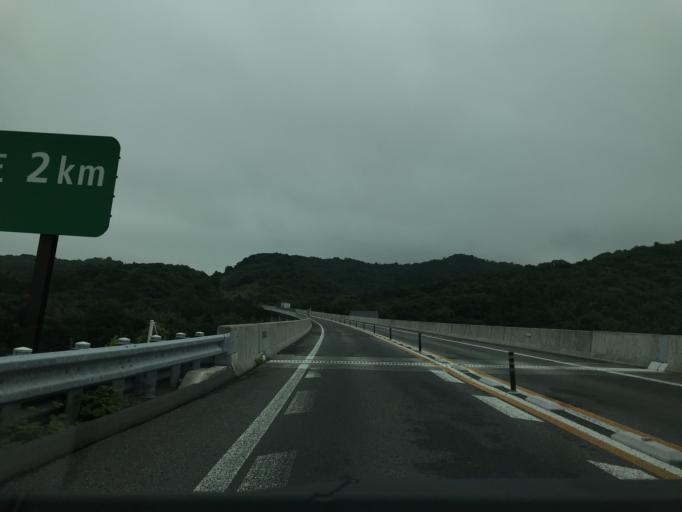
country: JP
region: Fukuoka
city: Nakatsu
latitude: 33.5049
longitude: 131.2976
